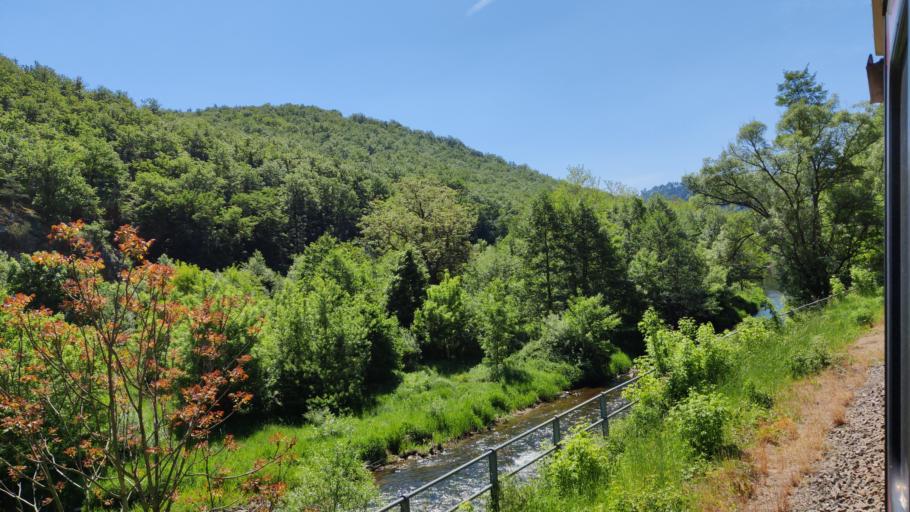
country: AT
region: Lower Austria
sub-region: Politischer Bezirk Horn
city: Horn
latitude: 48.6240
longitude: 15.6433
